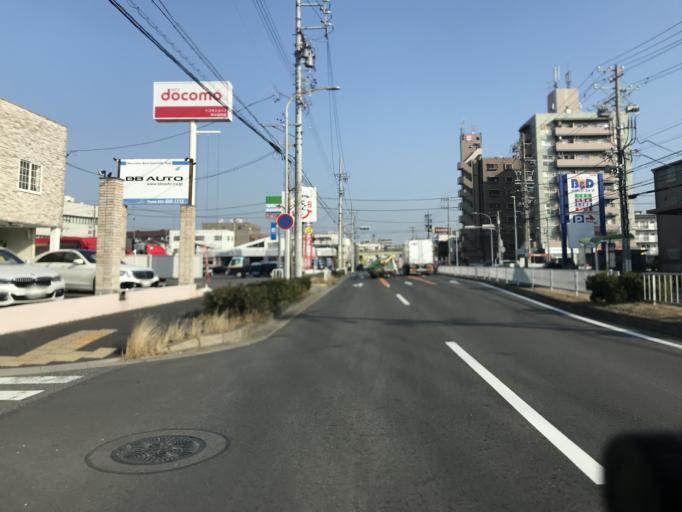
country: JP
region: Aichi
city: Nagoya-shi
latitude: 35.2123
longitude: 136.8699
